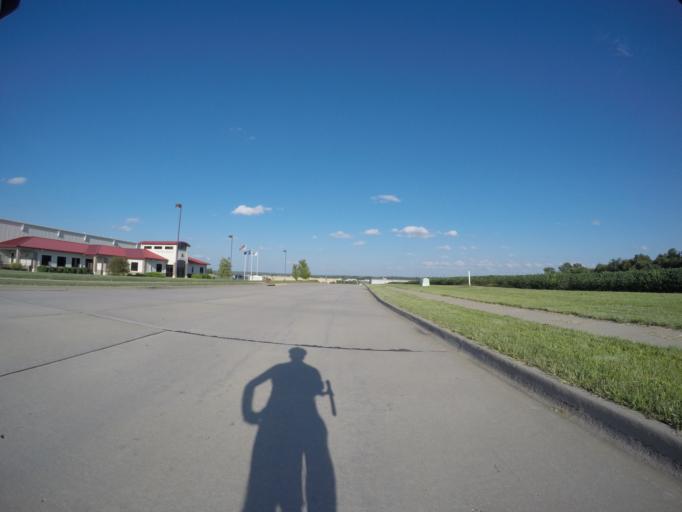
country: US
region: Kansas
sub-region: Riley County
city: Ogden
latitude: 39.1397
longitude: -96.6812
